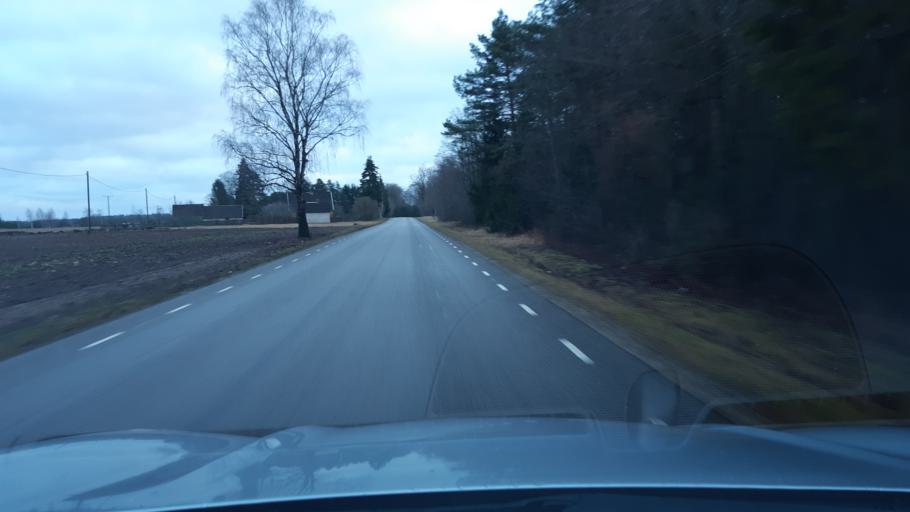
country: EE
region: Harju
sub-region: Saue linn
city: Saue
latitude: 59.2325
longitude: 24.5073
